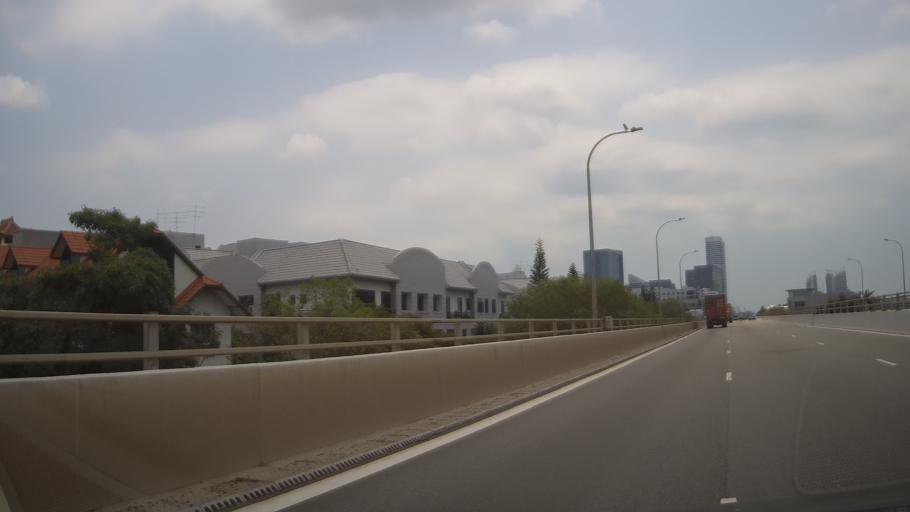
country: SG
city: Singapore
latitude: 1.2781
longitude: 103.7875
